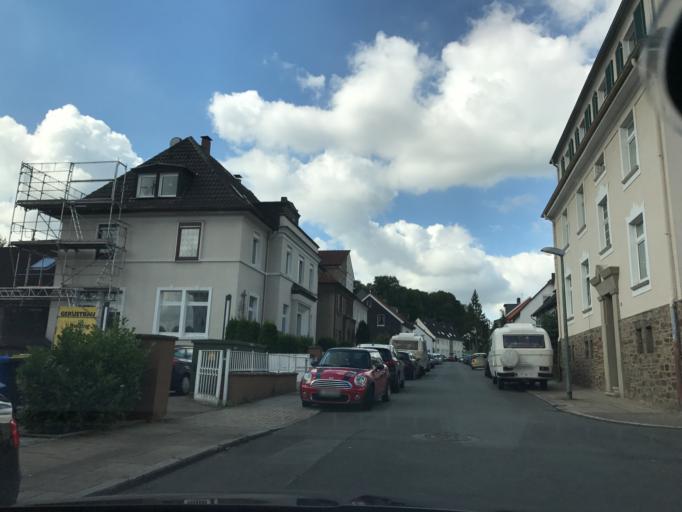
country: DE
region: North Rhine-Westphalia
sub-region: Regierungsbezirk Dusseldorf
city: Essen
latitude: 51.4215
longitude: 7.0376
